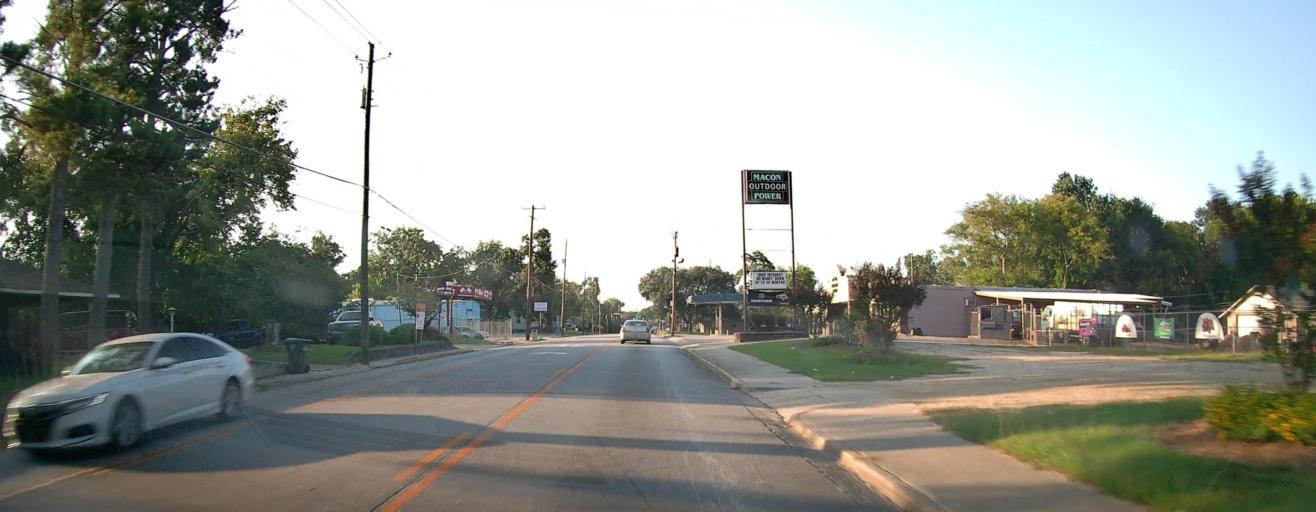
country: US
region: Georgia
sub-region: Bibb County
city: Macon
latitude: 32.8508
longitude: -83.6878
